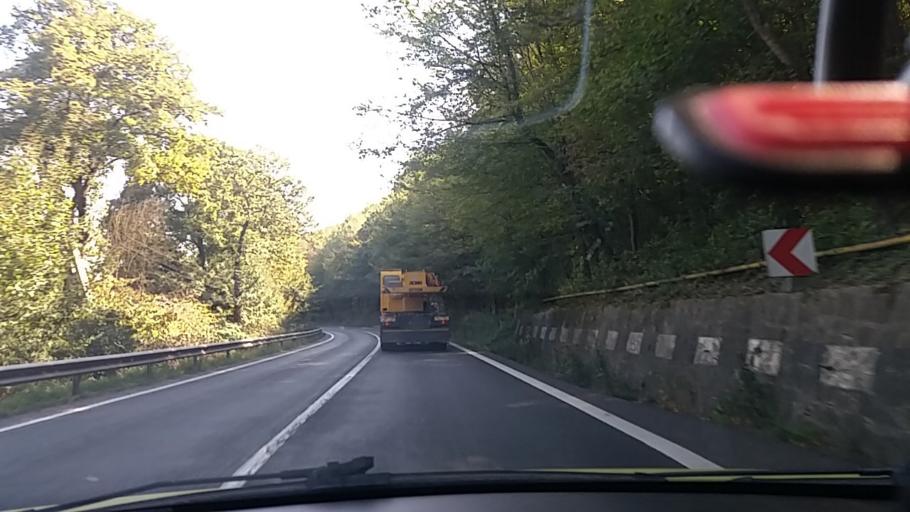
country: RO
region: Hunedoara
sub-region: Comuna Branisca
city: Branisca
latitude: 45.9062
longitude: 22.7763
